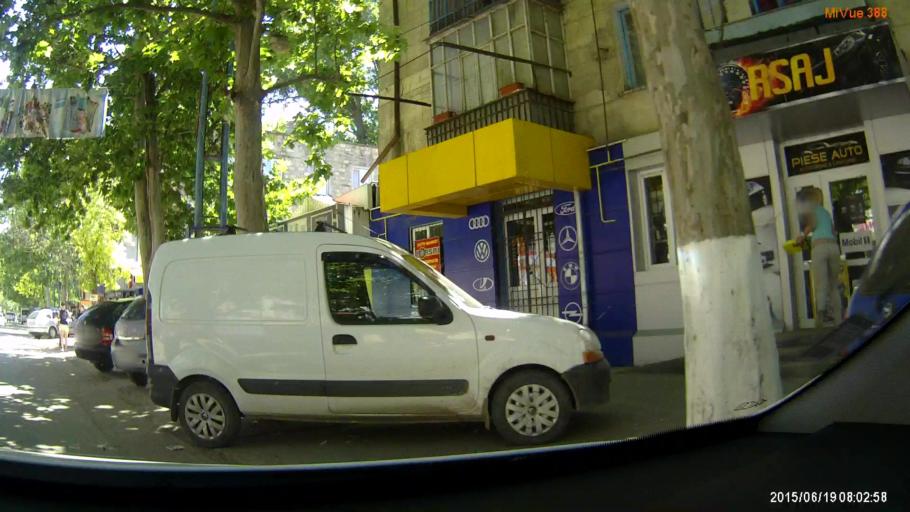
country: MD
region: Cahul
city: Cahul
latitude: 45.9087
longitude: 28.1927
